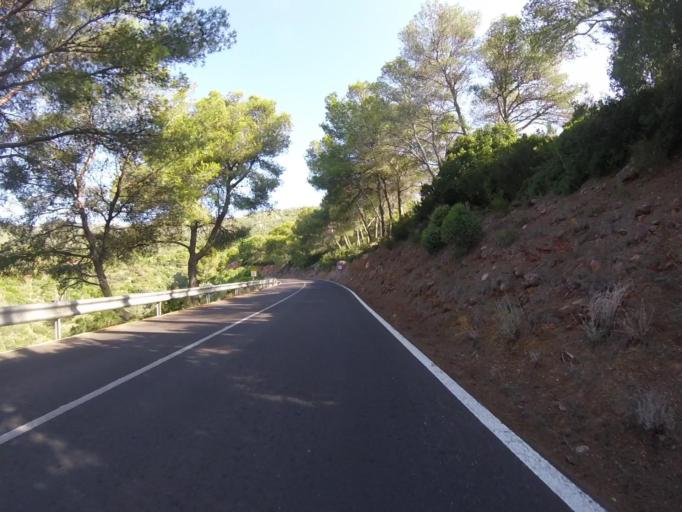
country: ES
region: Valencia
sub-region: Provincia de Castello
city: Benicassim
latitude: 40.0777
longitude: 0.0438
